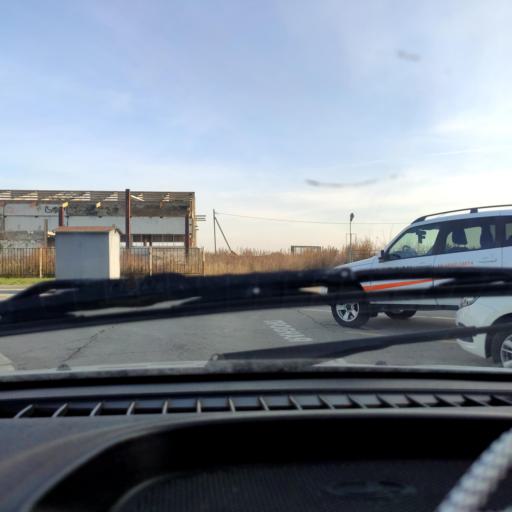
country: RU
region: Samara
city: Tol'yatti
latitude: 53.5707
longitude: 49.4692
